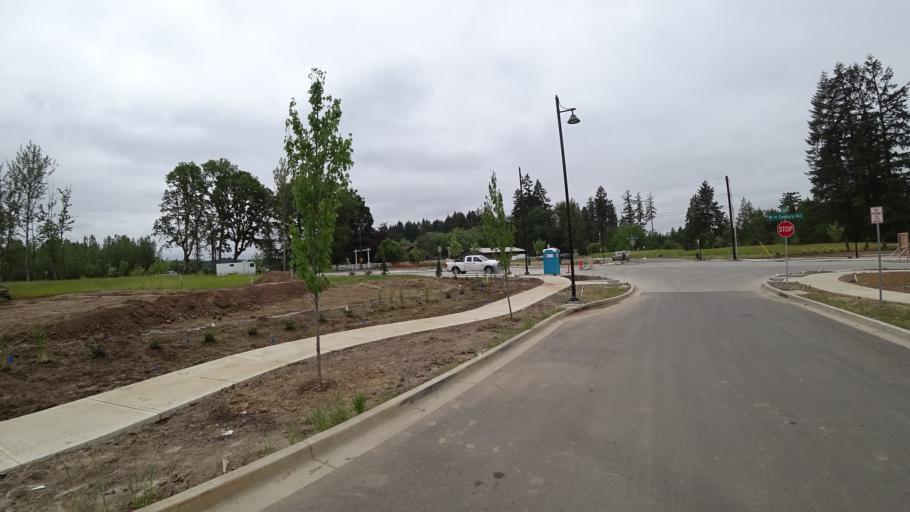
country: US
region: Oregon
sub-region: Washington County
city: Aloha
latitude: 45.4928
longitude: -122.9189
